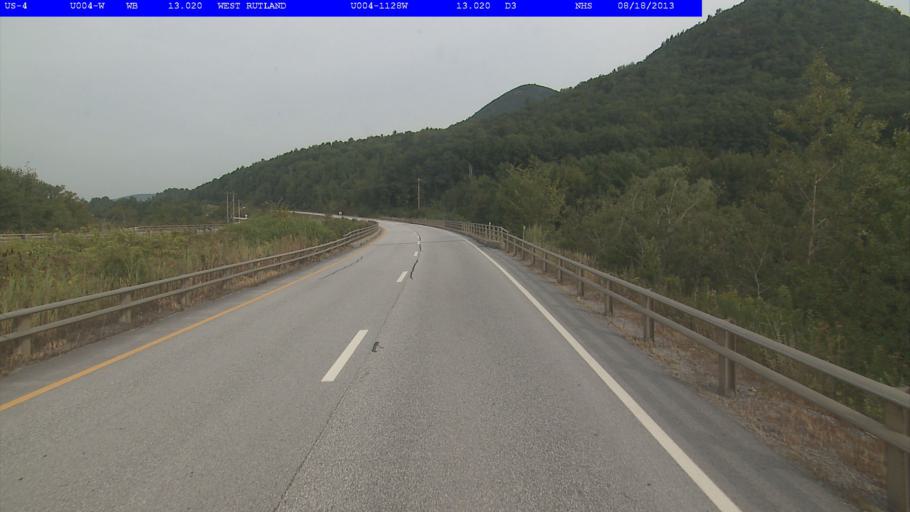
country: US
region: Vermont
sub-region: Rutland County
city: West Rutland
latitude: 43.6049
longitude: -73.0654
